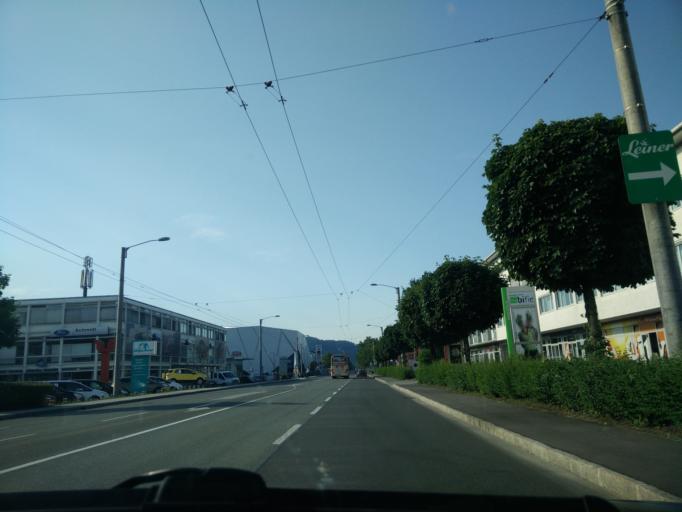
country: AT
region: Salzburg
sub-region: Politischer Bezirk Salzburg-Umgebung
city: Anif
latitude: 47.7716
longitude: 13.0696
